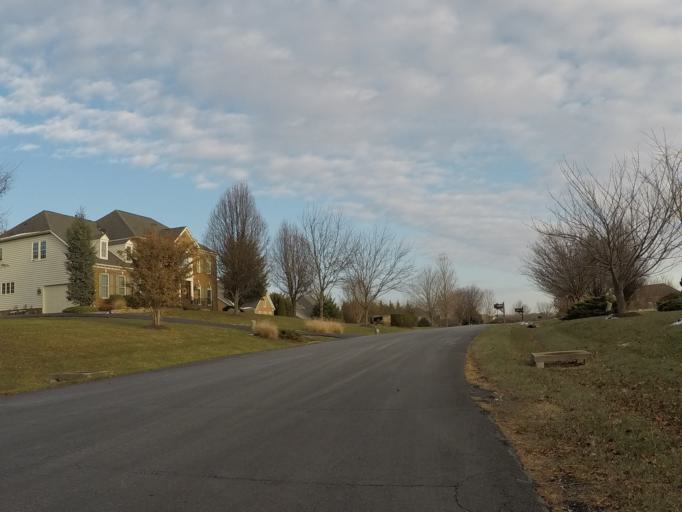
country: US
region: Maryland
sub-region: Howard County
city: Columbia
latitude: 39.2861
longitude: -76.9083
